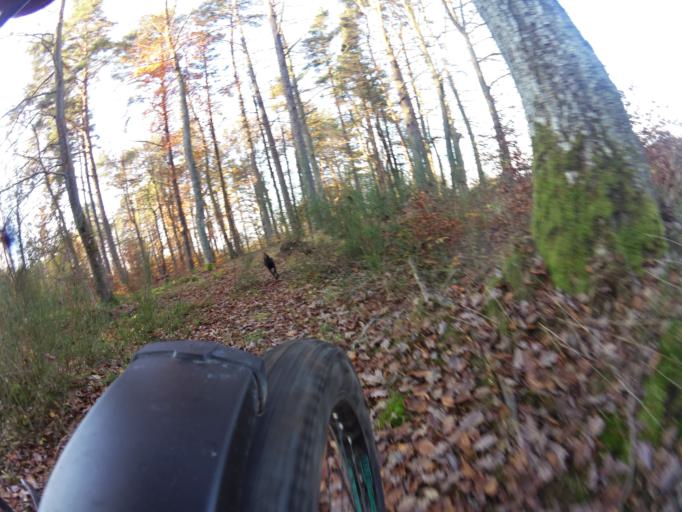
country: PL
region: Pomeranian Voivodeship
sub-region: Powiat pucki
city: Krokowa
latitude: 54.7300
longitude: 18.1984
